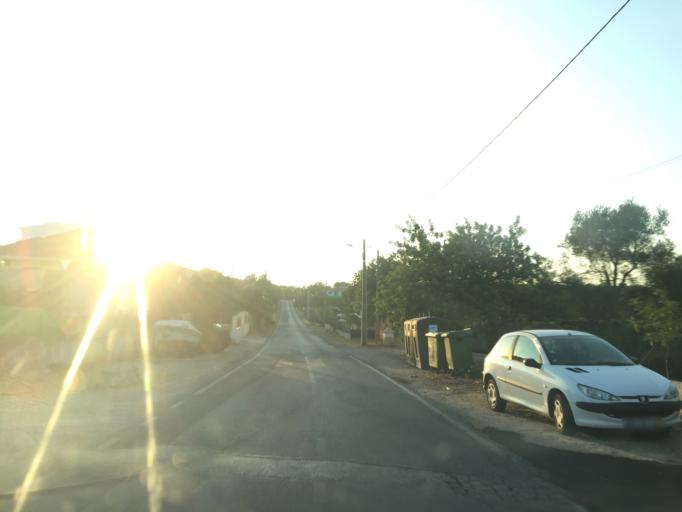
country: PT
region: Faro
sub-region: Sao Bras de Alportel
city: Sao Bras de Alportel
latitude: 37.0869
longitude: -7.8813
